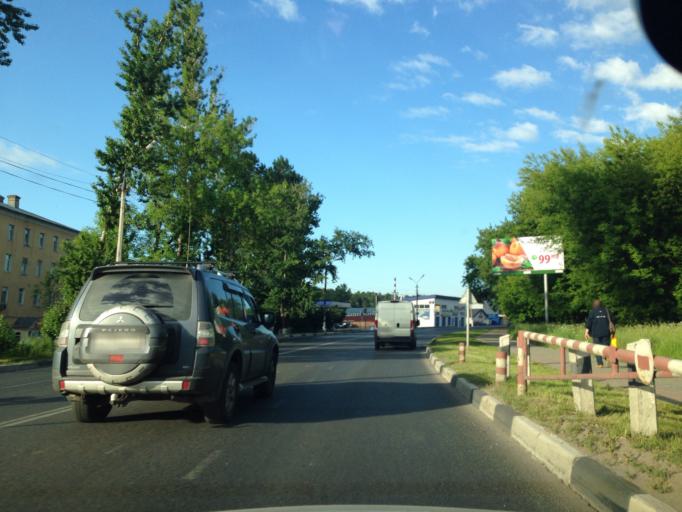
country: RU
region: Moskovskaya
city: Balashikha
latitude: 55.8119
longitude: 37.9532
